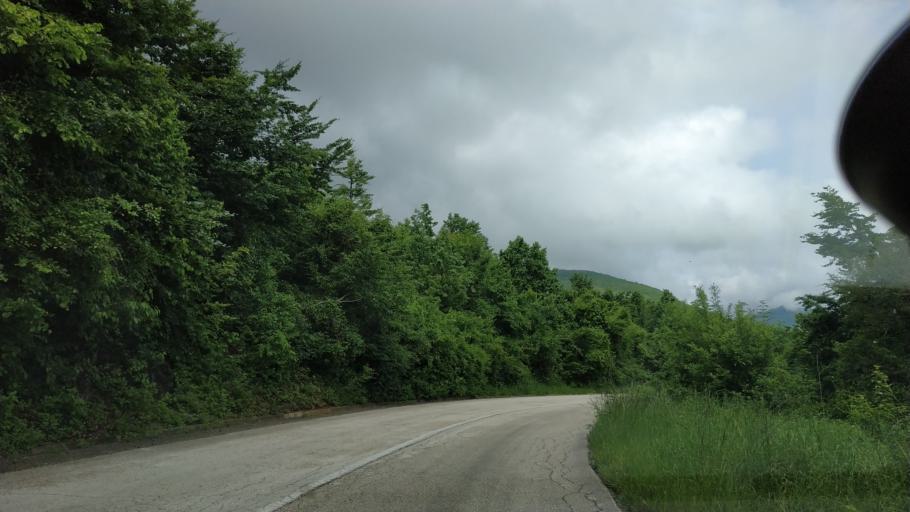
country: RS
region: Central Serbia
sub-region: Zajecarski Okrug
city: Boljevac
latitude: 43.7259
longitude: 21.9525
